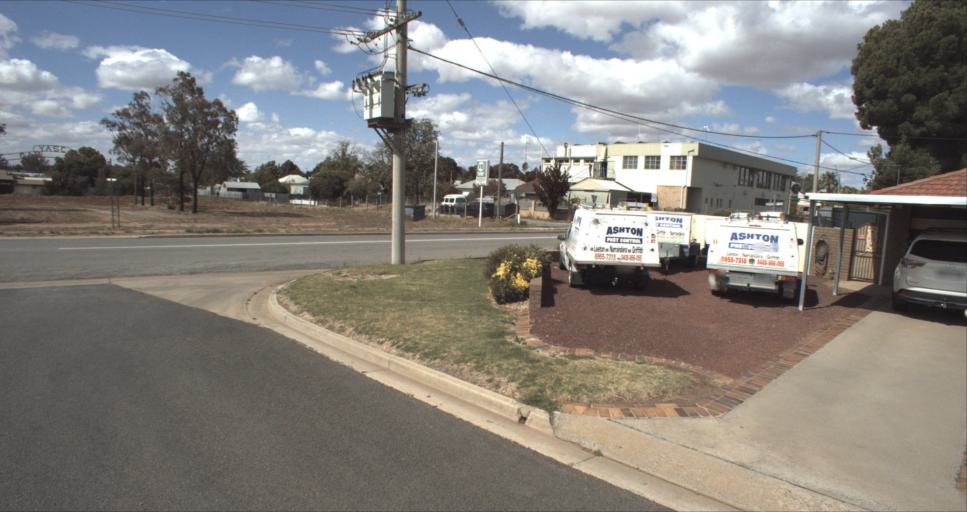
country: AU
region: New South Wales
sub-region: Leeton
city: Leeton
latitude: -34.6032
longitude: 146.4087
